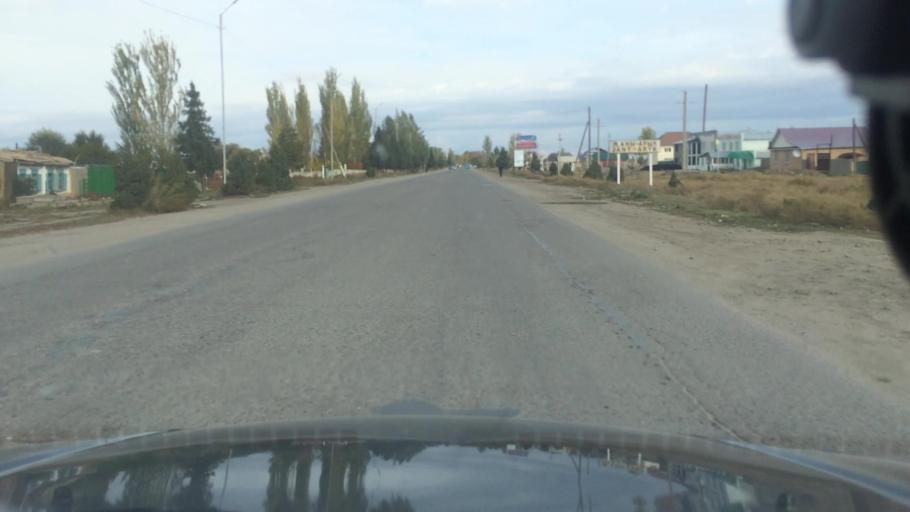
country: KG
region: Ysyk-Koel
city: Karakol
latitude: 42.5240
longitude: 78.3853
